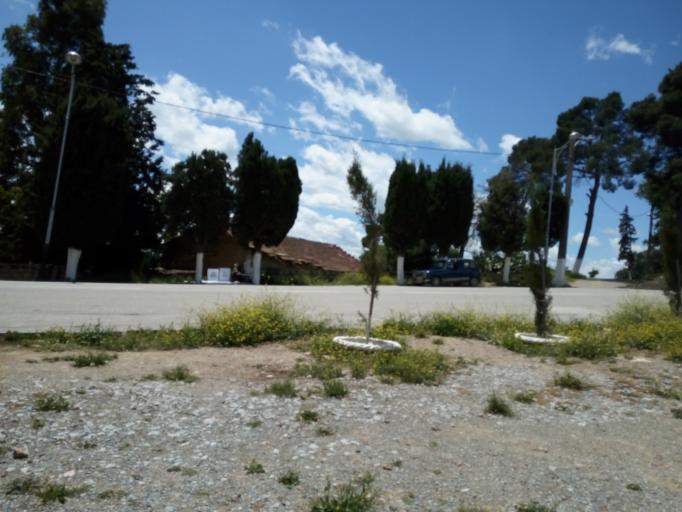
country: DZ
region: Constantine
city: Constantine
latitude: 36.3752
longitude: 6.6144
